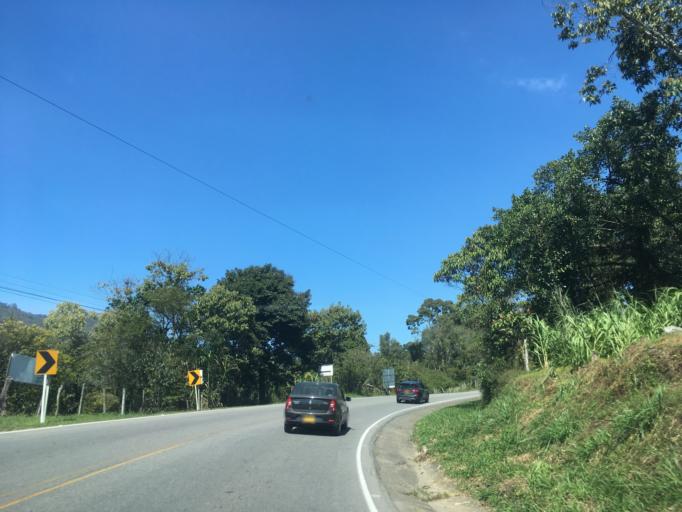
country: CO
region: Santander
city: Suaita
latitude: 6.0732
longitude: -73.4080
